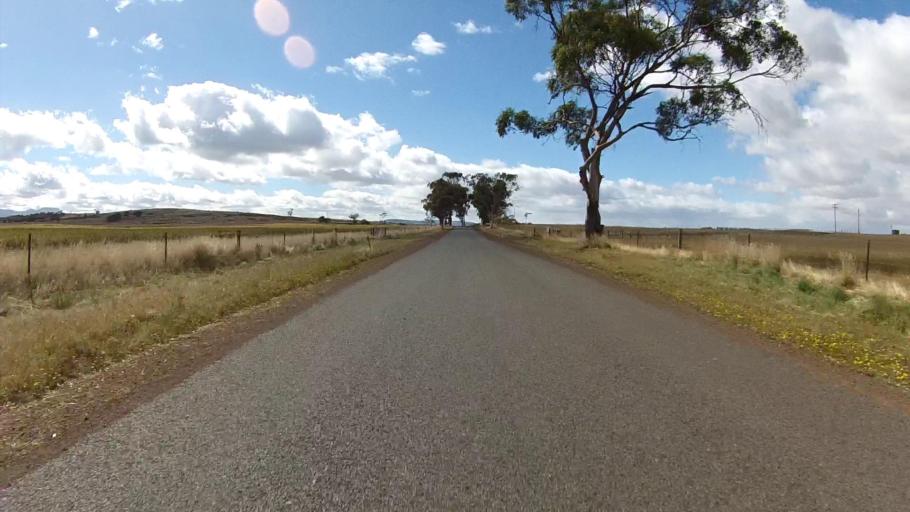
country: AU
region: Tasmania
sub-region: Northern Midlands
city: Evandale
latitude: -41.7012
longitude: 147.3800
